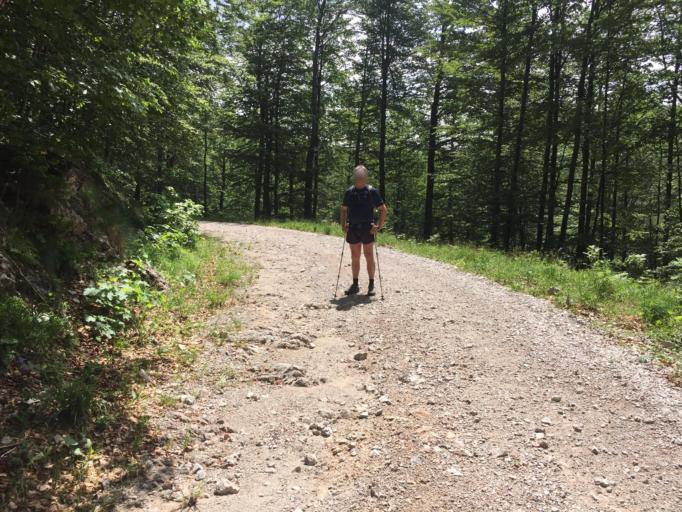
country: HR
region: Primorsko-Goranska
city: Krasica
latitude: 45.4239
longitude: 14.6039
